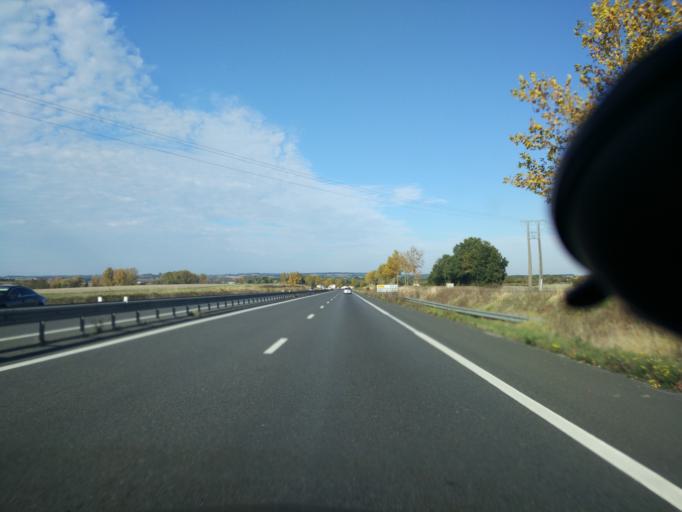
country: FR
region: Poitou-Charentes
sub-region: Departement de la Charente
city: Barbezieux-Saint-Hilaire
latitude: 45.4844
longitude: -0.1306
